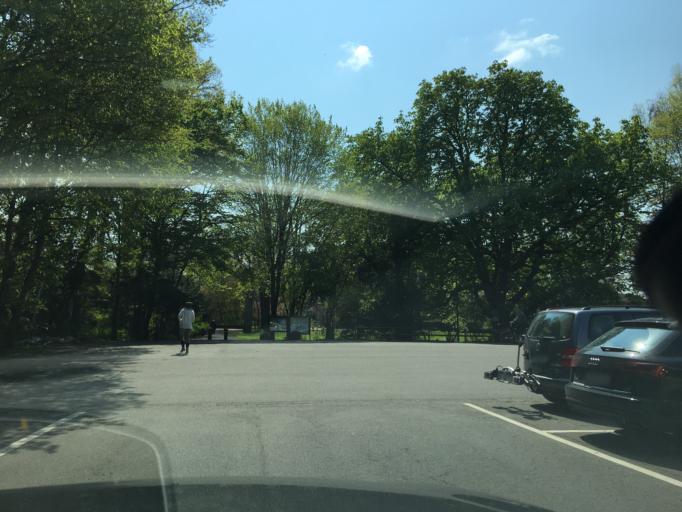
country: DE
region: North Rhine-Westphalia
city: Ludinghausen
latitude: 51.7772
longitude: 7.4405
